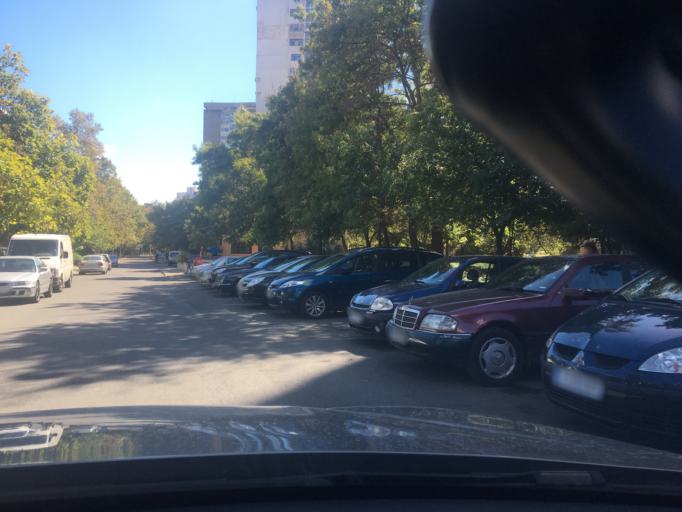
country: BG
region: Burgas
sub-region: Obshtina Burgas
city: Burgas
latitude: 42.5064
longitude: 27.4741
